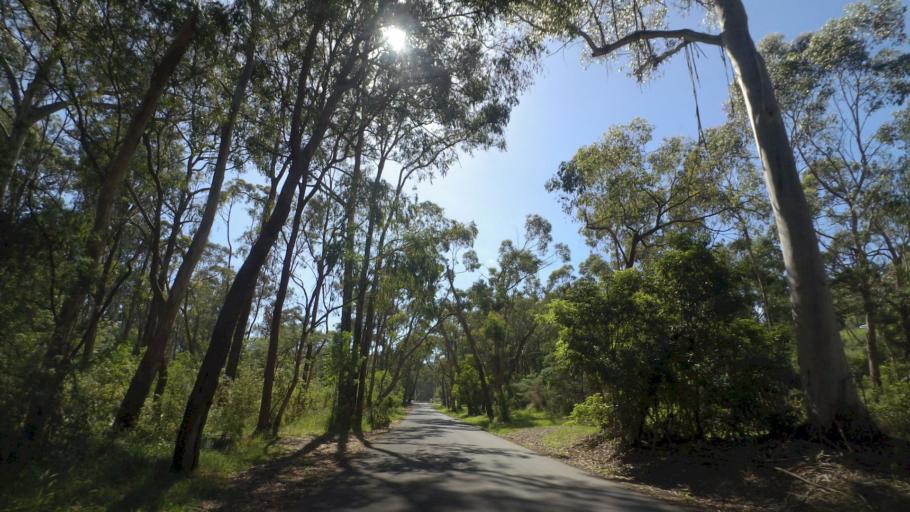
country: AU
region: Victoria
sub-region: Yarra Ranges
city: Mount Evelyn
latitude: -37.7962
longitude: 145.3791
